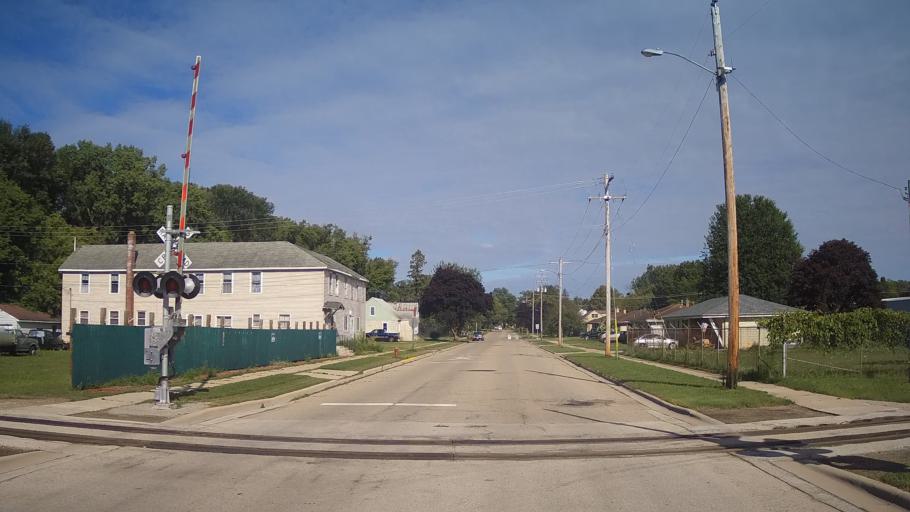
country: US
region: Wisconsin
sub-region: Oconto County
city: Oconto
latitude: 44.8902
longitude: -87.8819
